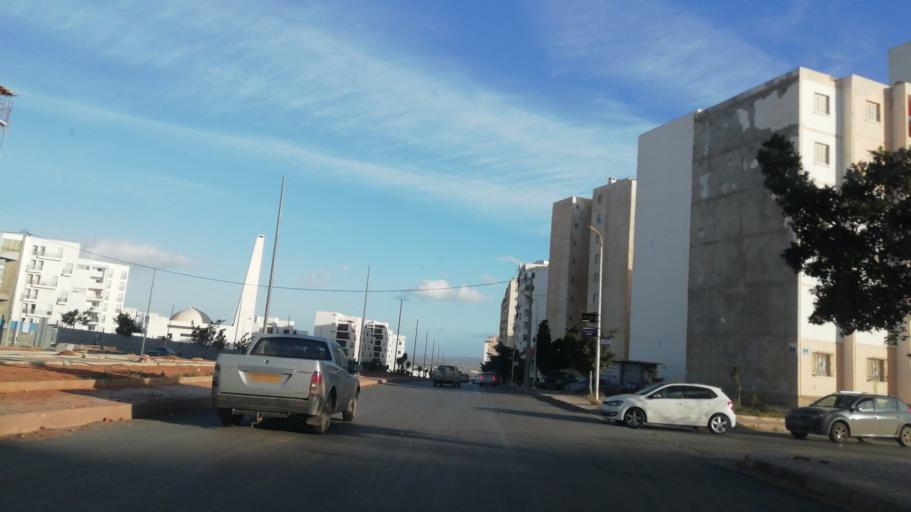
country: DZ
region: Oran
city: Bir el Djir
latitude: 35.7071
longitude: -0.5603
